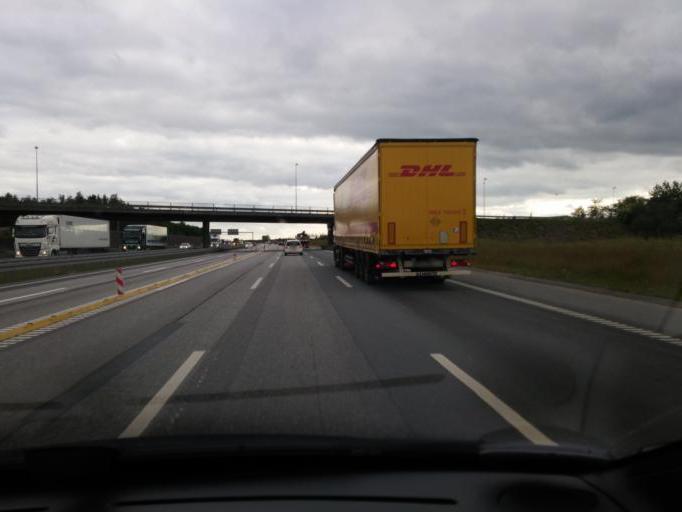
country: DK
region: Zealand
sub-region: Solrod Kommune
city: Solrod Strand
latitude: 55.5740
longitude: 12.2465
